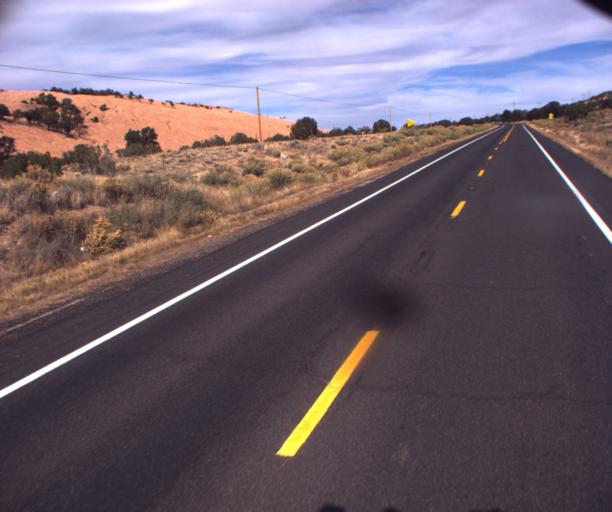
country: US
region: Arizona
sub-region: Navajo County
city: Kayenta
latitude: 36.6388
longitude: -110.4409
